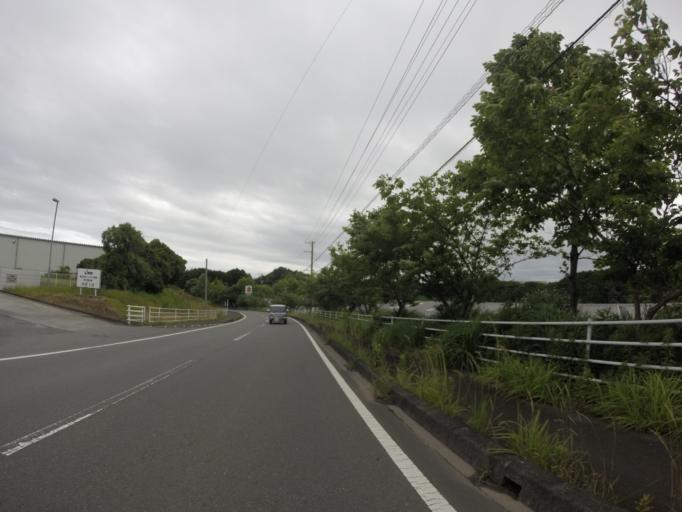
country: JP
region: Shizuoka
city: Sagara
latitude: 34.7339
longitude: 138.1853
